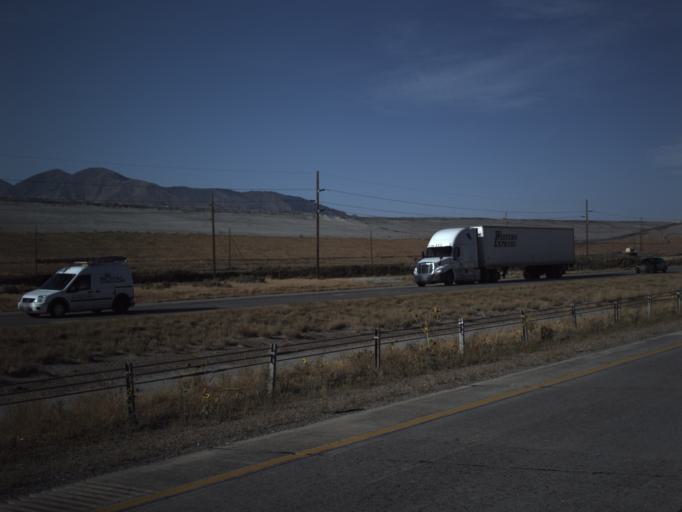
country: US
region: Utah
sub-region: Salt Lake County
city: Magna
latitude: 40.7710
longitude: -112.1137
